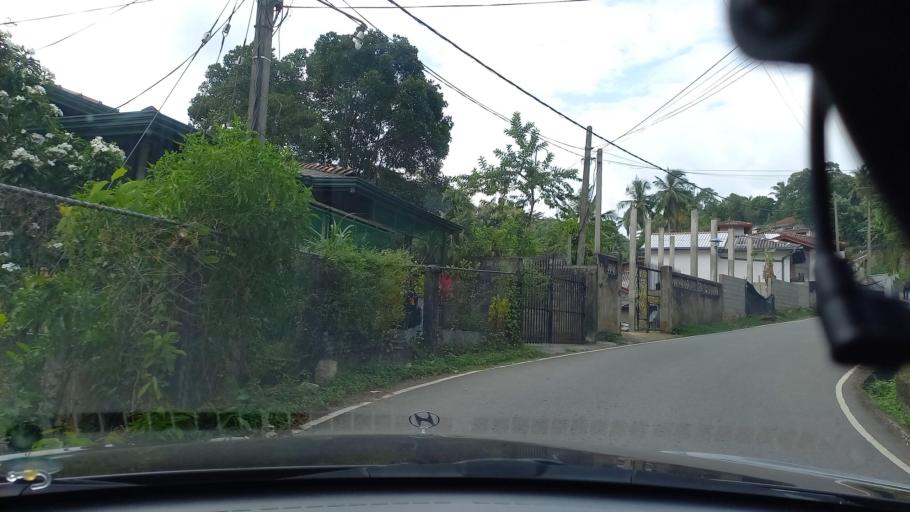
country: LK
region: Central
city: Kadugannawa
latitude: 7.2580
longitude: 80.3548
